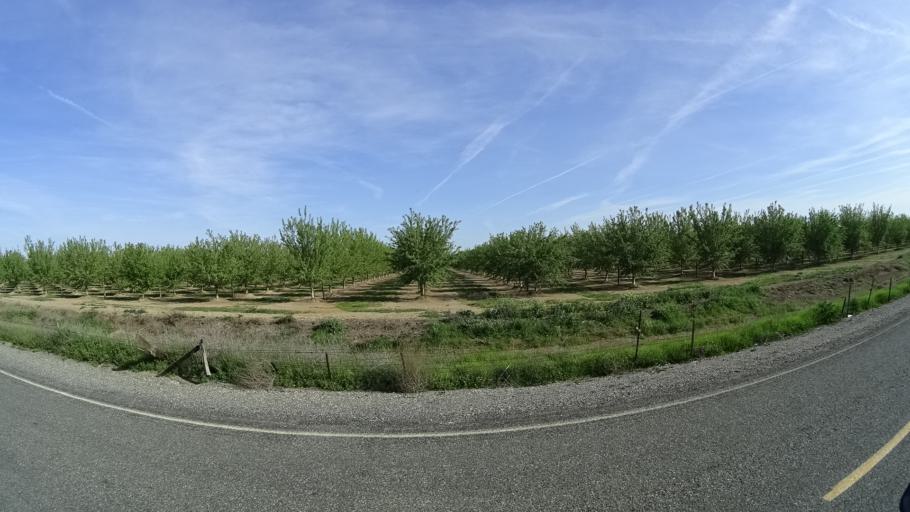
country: US
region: California
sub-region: Glenn County
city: Orland
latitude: 39.6682
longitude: -122.2480
